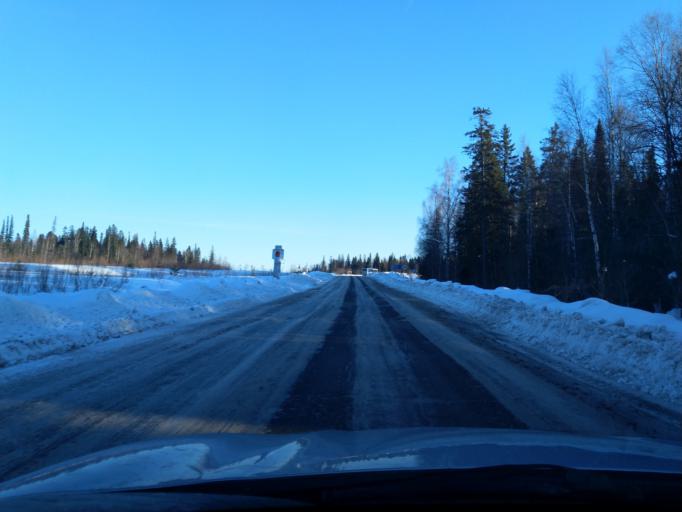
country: RU
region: Perm
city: Polazna
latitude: 58.2965
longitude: 56.4783
